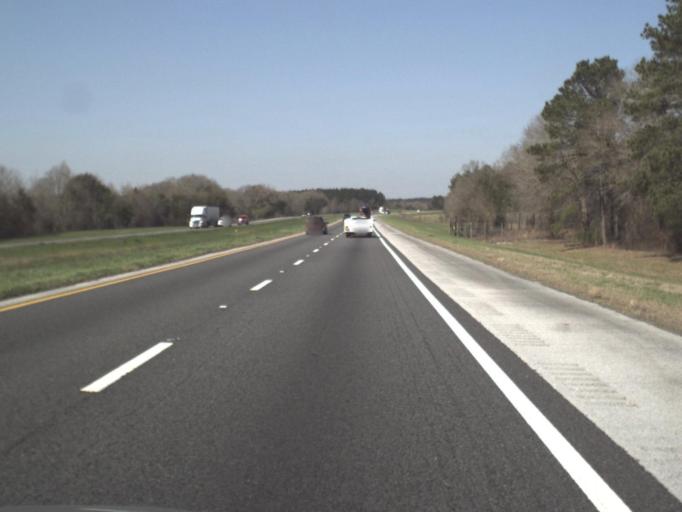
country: US
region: Florida
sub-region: Jackson County
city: Marianna
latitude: 30.6835
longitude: -85.1012
